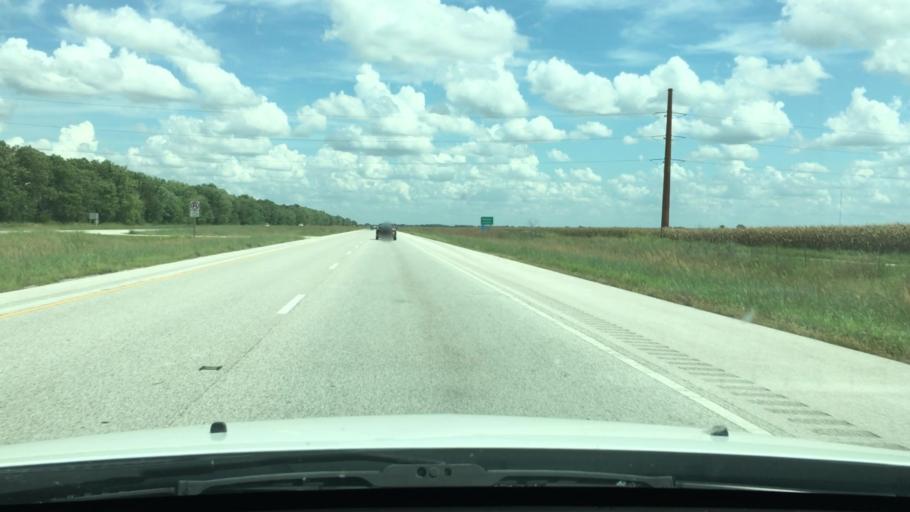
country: US
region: Illinois
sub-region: Scott County
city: Winchester
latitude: 39.6801
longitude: -90.3743
